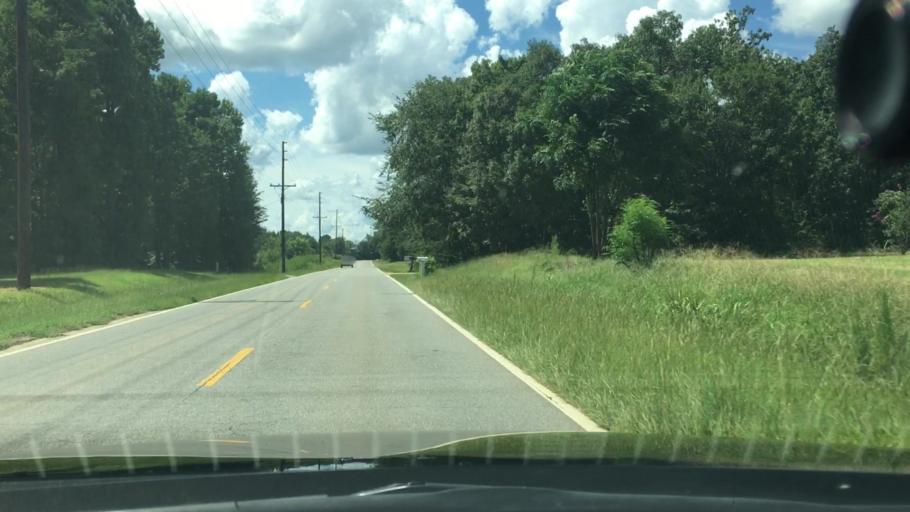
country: US
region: Georgia
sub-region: Putnam County
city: Jefferson
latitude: 33.3624
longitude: -83.2670
